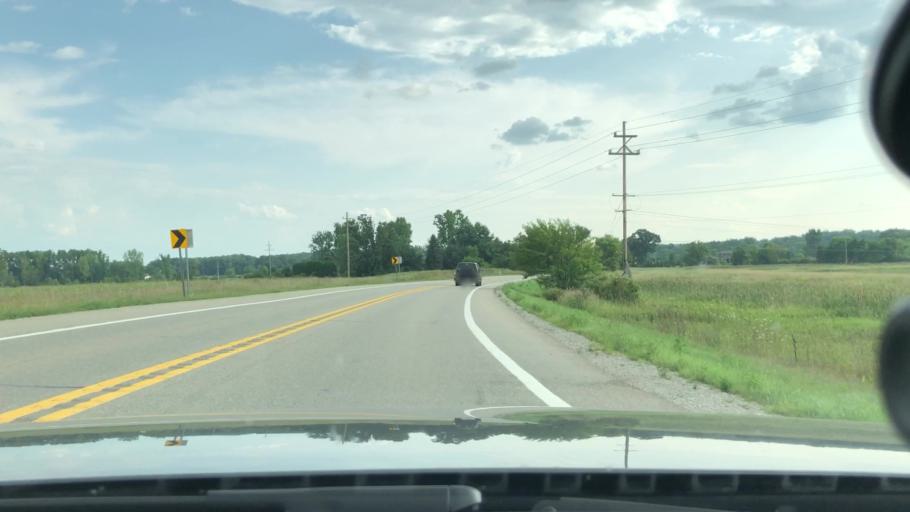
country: US
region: Michigan
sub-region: Washtenaw County
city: Chelsea
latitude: 42.2473
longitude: -84.0335
